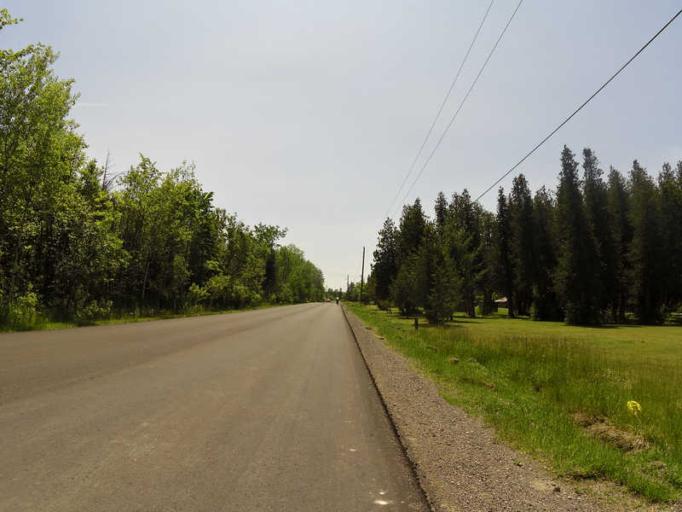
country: CA
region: Ontario
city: Peterborough
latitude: 44.3657
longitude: -78.2900
